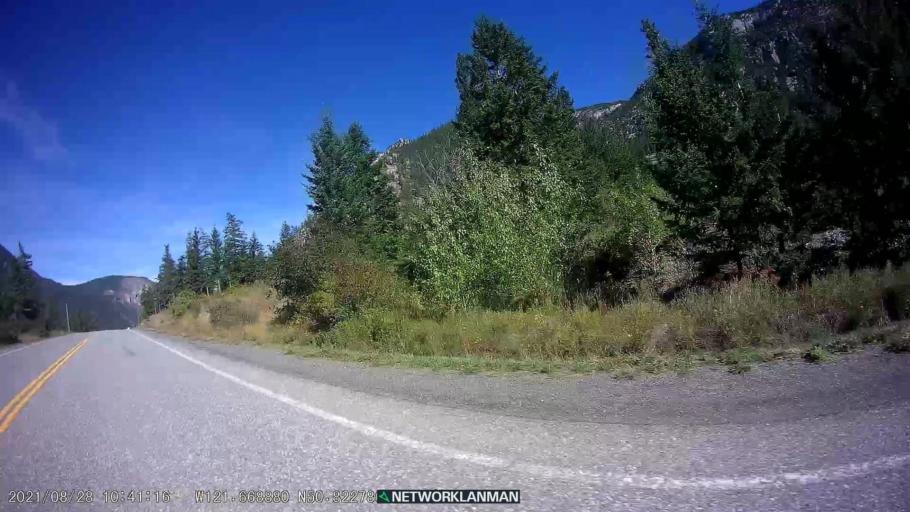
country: CA
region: British Columbia
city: Lillooet
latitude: 50.8230
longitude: -121.6694
